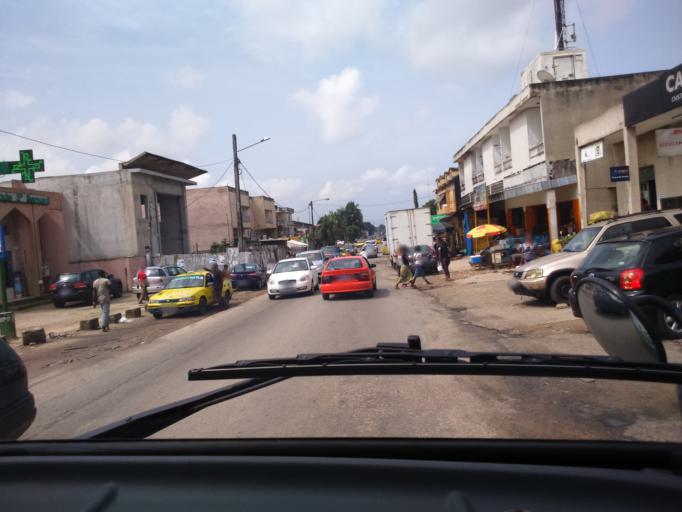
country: CI
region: Lagunes
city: Abobo
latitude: 5.3674
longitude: -3.9797
